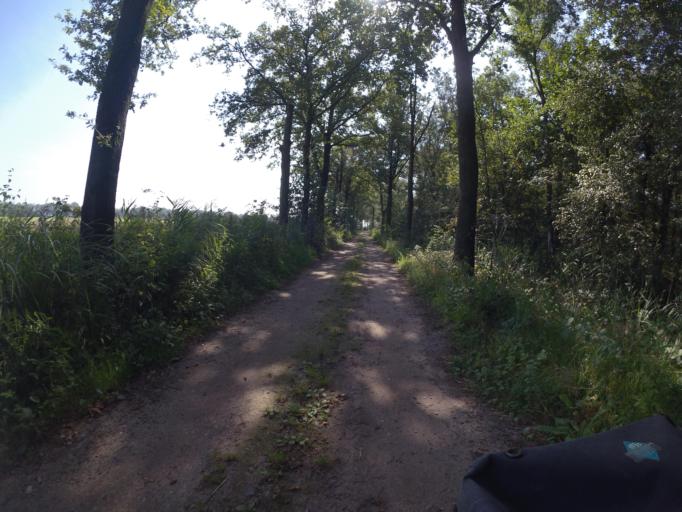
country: NL
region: North Brabant
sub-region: Gemeente Oirschot
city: Oirschot
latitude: 51.5486
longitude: 5.2775
